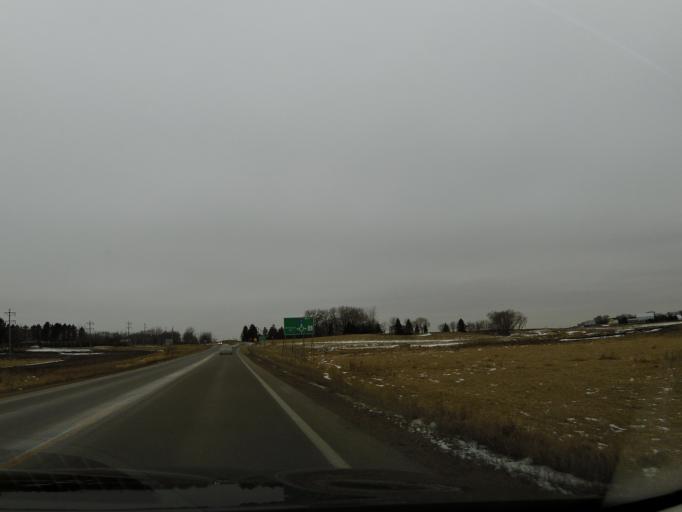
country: US
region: Minnesota
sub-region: Carver County
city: Waconia
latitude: 44.8310
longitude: -93.8192
